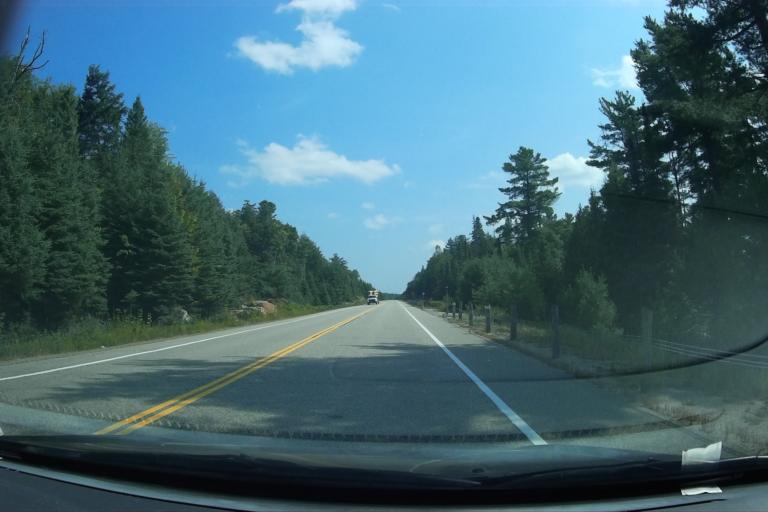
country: CA
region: Ontario
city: Huntsville
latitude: 45.5660
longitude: -78.5601
